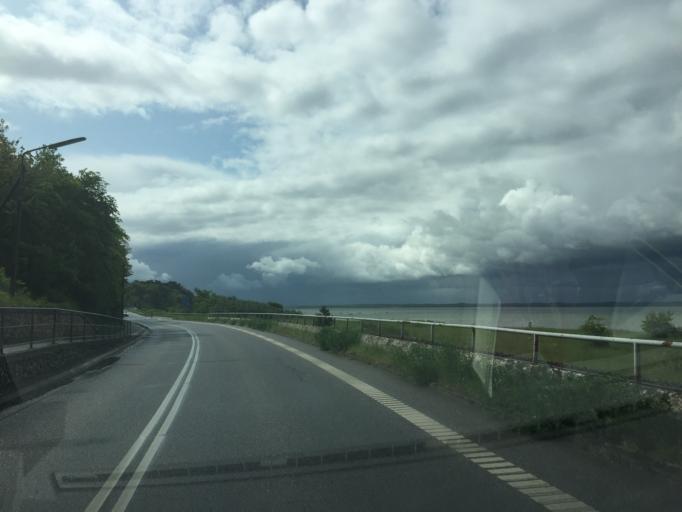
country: DK
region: Capital Region
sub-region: Halsnaes Kommune
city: Frederiksvaerk
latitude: 55.9590
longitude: 12.0197
